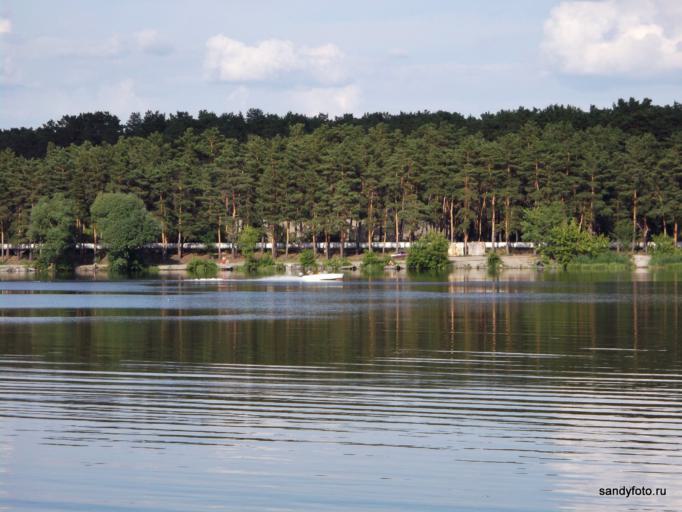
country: RU
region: Chelyabinsk
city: Troitsk
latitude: 54.0511
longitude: 61.6096
